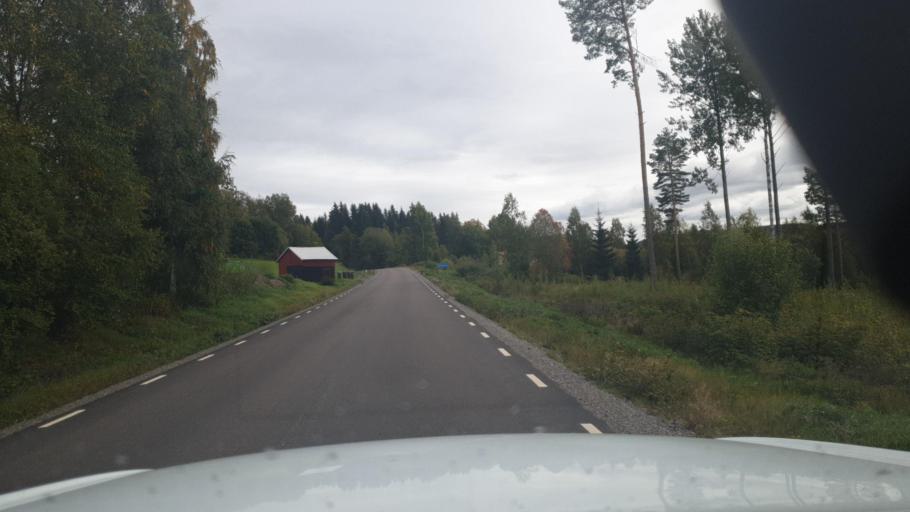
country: SE
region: Vaermland
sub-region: Torsby Kommun
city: Torsby
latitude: 59.9868
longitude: 12.7575
